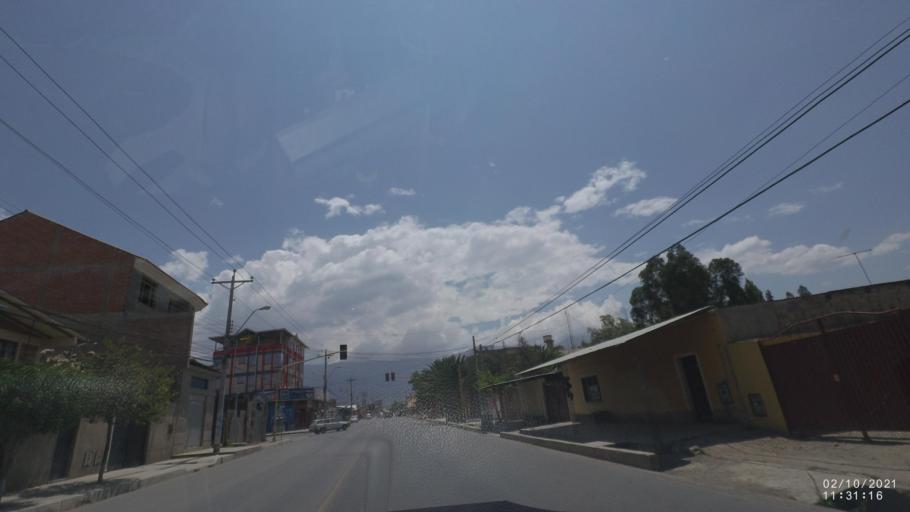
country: BO
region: Cochabamba
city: Cochabamba
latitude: -17.3853
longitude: -66.2369
